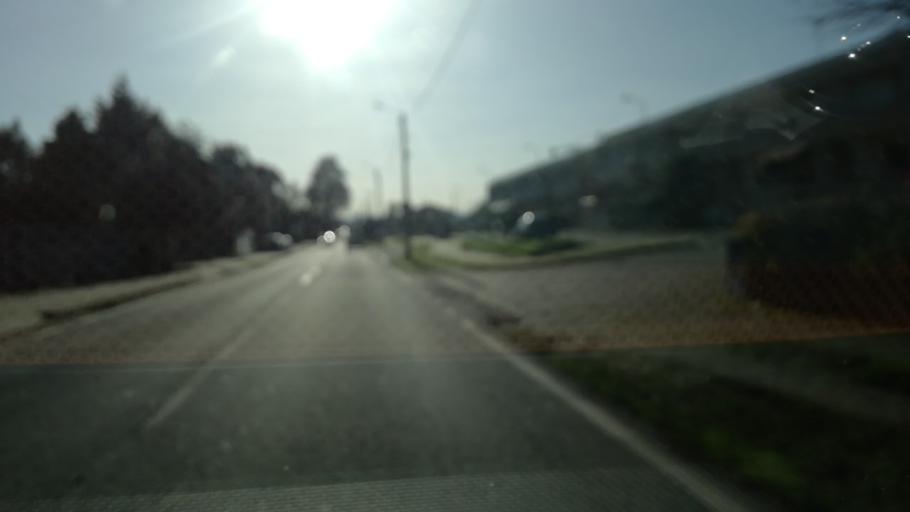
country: PT
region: Braga
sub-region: Guimaraes
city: Ponte
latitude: 41.5076
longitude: -8.3204
